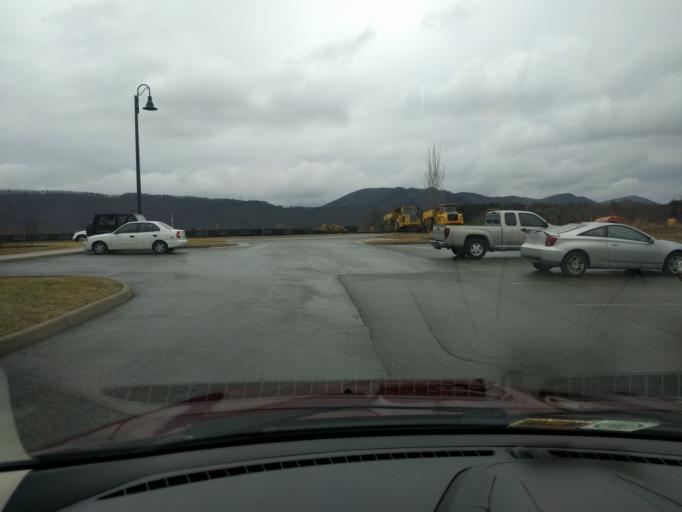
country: US
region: Virginia
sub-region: Botetourt County
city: Daleville
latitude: 37.4167
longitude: -79.9147
